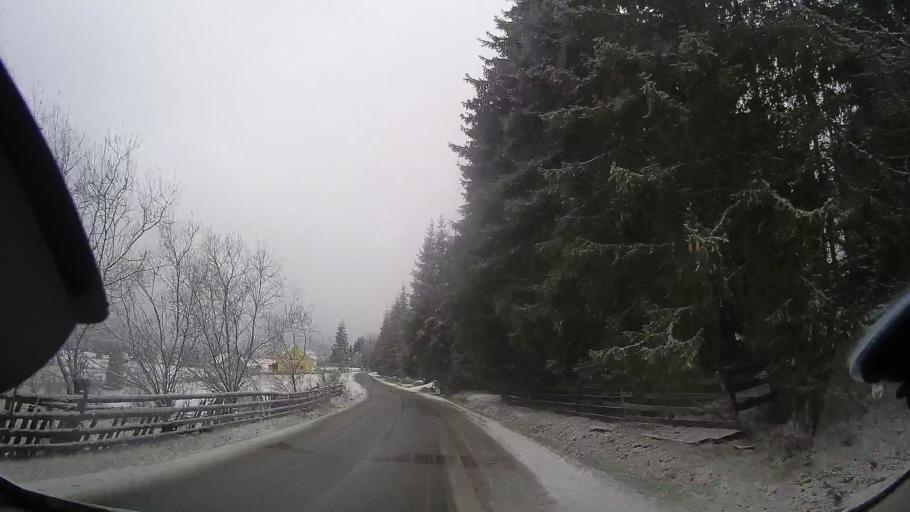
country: RO
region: Cluj
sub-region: Comuna Maguri-Racatau
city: Maguri
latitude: 46.6570
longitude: 23.0874
